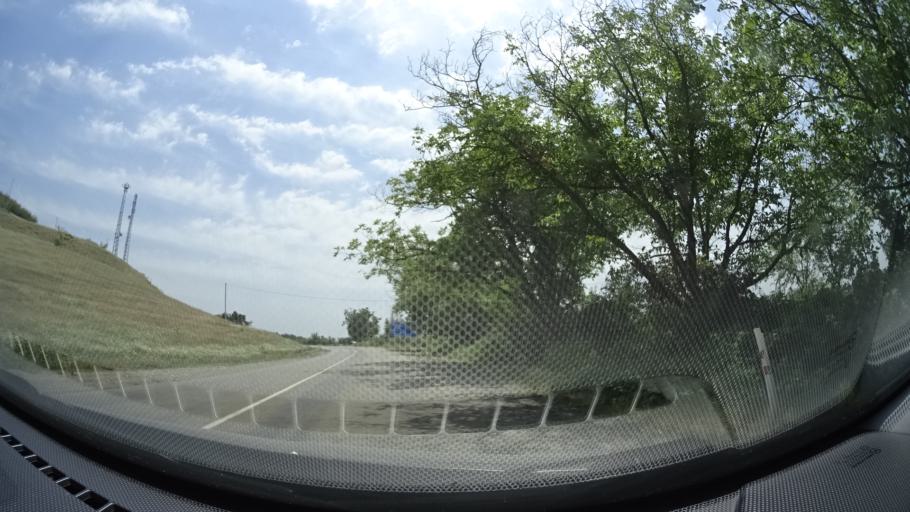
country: GE
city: Bagdadi
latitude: 41.8377
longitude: 46.0933
